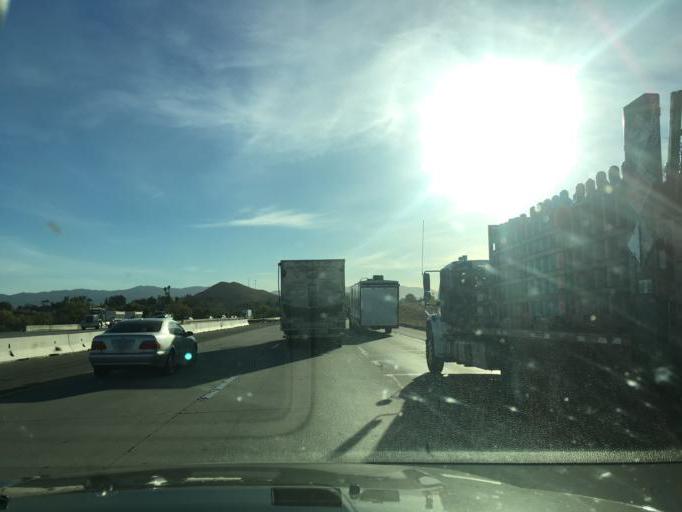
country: US
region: California
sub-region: Riverside County
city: Norco
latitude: 33.9514
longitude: -117.5514
